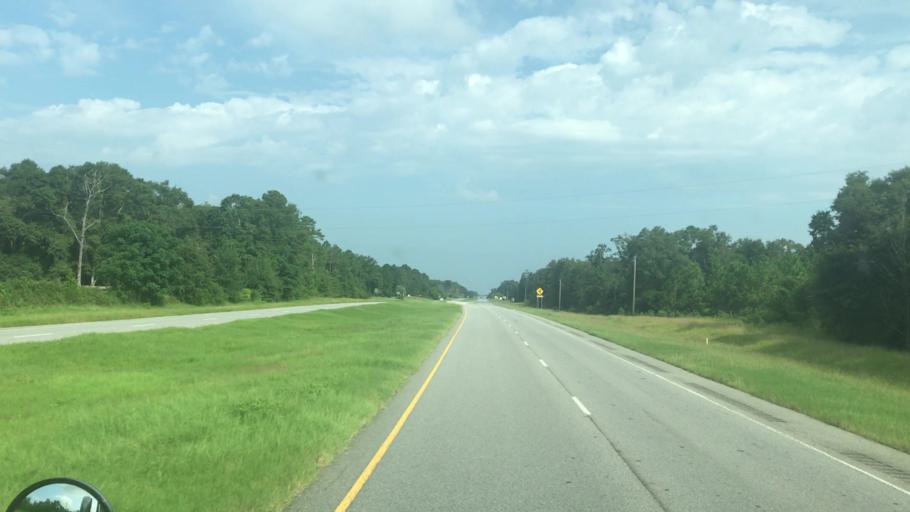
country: US
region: Georgia
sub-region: Early County
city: Blakely
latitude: 31.2866
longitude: -84.8442
